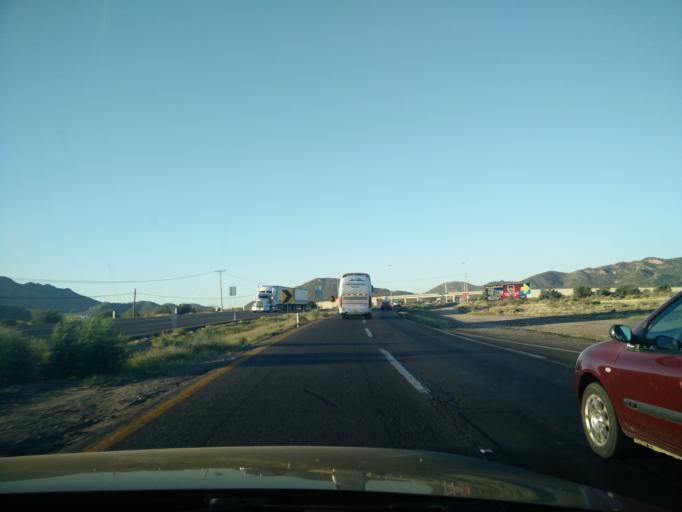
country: MX
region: Sonora
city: Hermosillo
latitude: 29.0139
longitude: -110.9622
